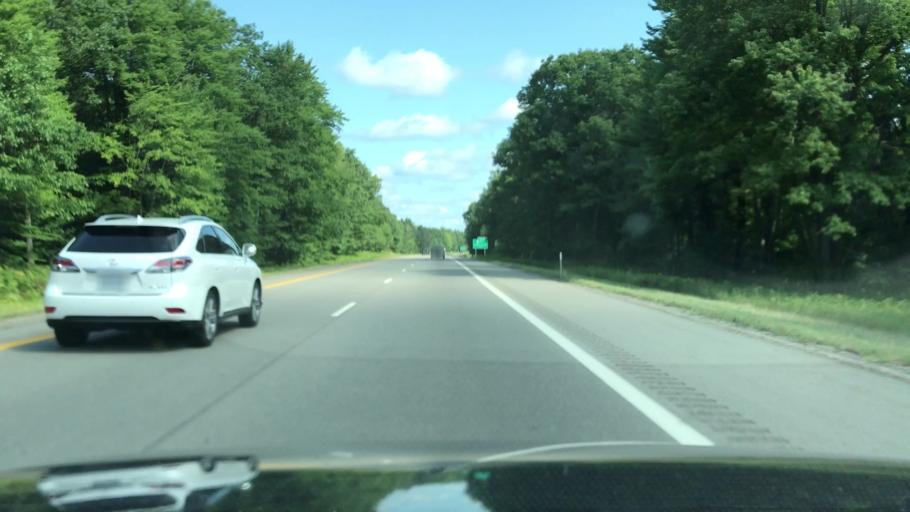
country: US
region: Michigan
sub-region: Mecosta County
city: Big Rapids
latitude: 43.5600
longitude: -85.4892
